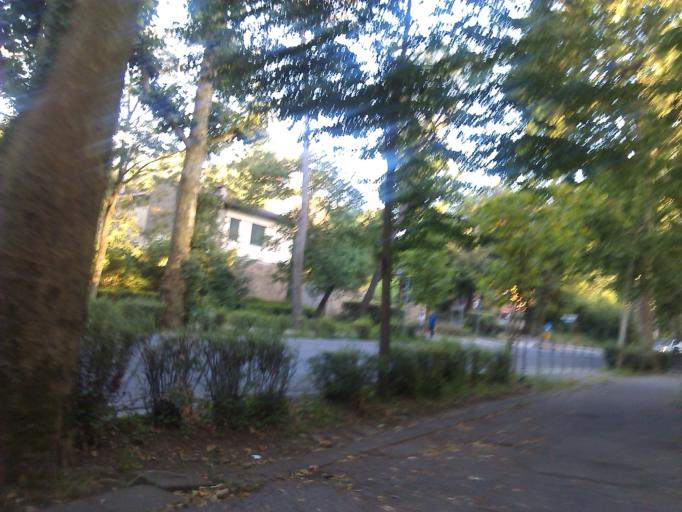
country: IT
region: Tuscany
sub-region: Province of Florence
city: Florence
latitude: 43.7585
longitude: 11.2715
